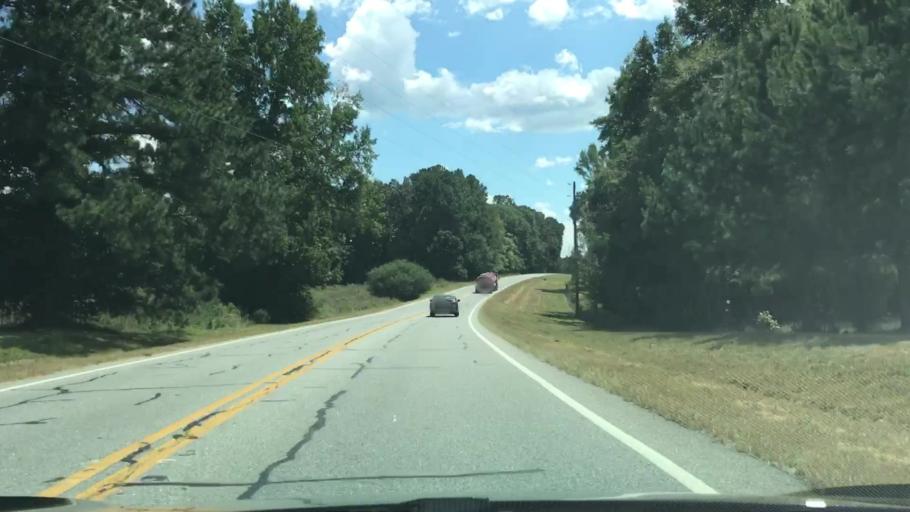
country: US
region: Georgia
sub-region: Oconee County
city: Watkinsville
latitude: 33.7511
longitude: -83.3018
